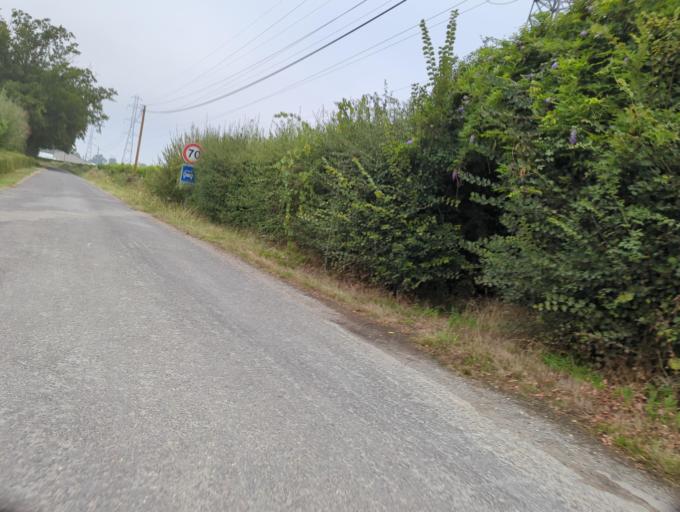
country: FR
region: Pays de la Loire
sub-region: Departement de Maine-et-Loire
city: Trelaze
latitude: 47.4814
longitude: -0.4802
